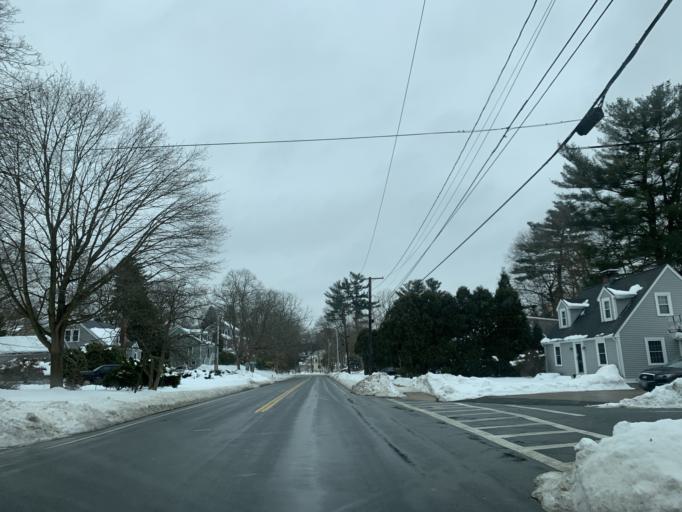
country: US
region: Massachusetts
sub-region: Norfolk County
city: Westwood
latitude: 42.2130
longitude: -71.2257
